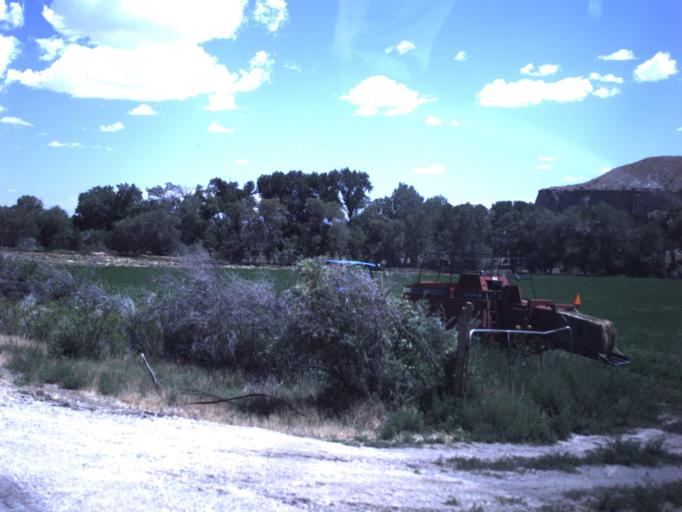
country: US
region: Utah
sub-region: Emery County
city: Orangeville
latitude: 39.2499
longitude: -111.0816
